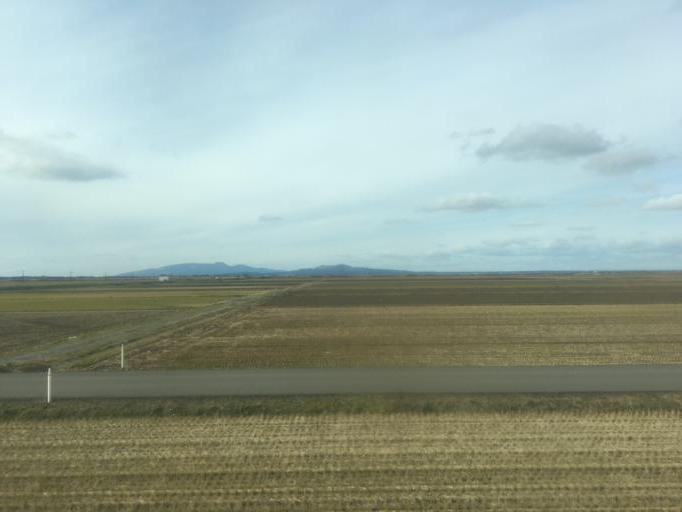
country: JP
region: Akita
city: Tenno
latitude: 39.8910
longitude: 140.0703
